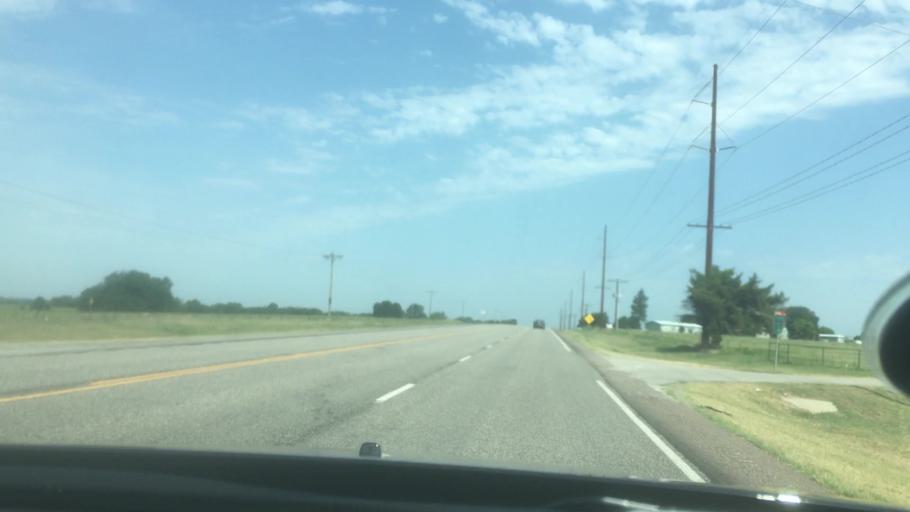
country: US
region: Oklahoma
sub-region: Seminole County
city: Konawa
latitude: 34.8497
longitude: -96.8094
